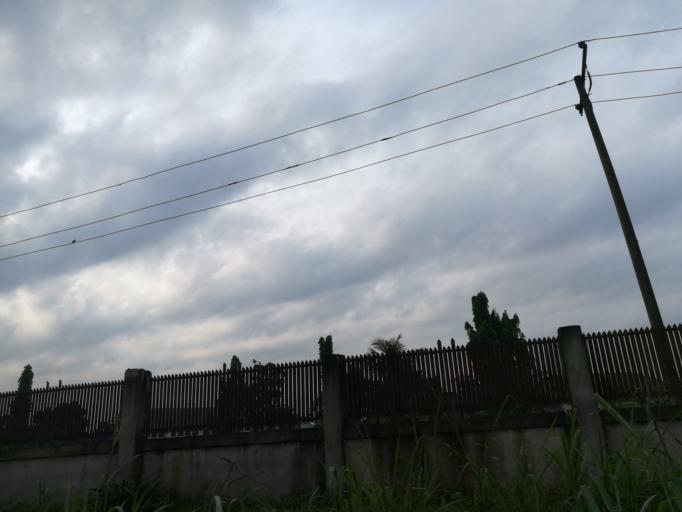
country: NG
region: Rivers
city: Port Harcourt
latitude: 4.8447
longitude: 7.0564
